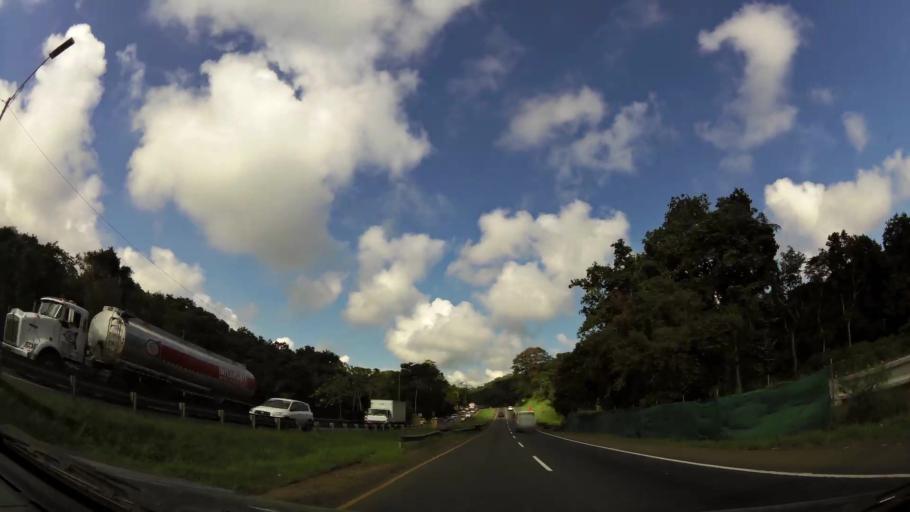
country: PA
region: Panama
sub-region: Distrito Arraijan
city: Arraijan
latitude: 8.9563
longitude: -79.6022
